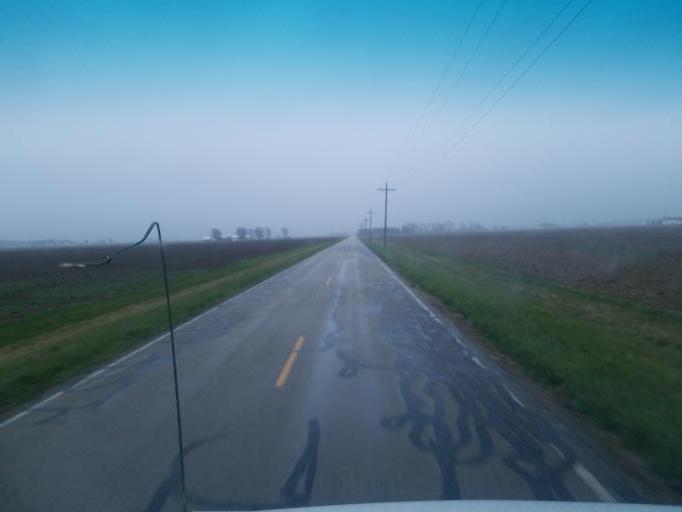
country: US
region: Ohio
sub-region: Henry County
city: Napoleon
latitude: 41.4133
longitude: -84.2401
